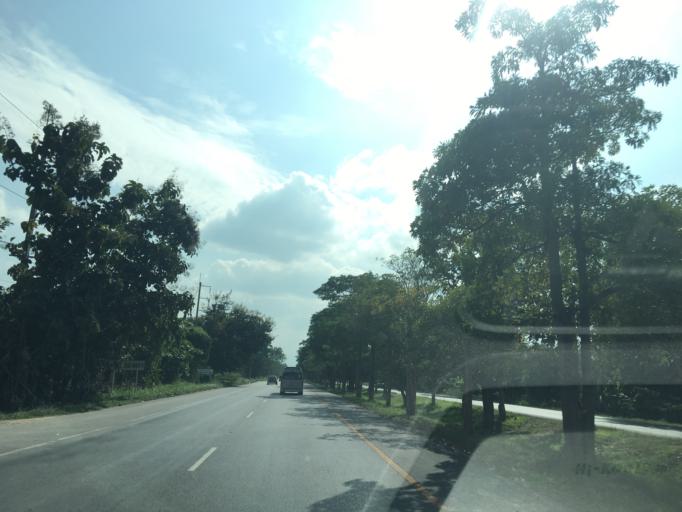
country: TH
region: Chiang Rai
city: Mae Lao
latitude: 19.7392
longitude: 99.7227
